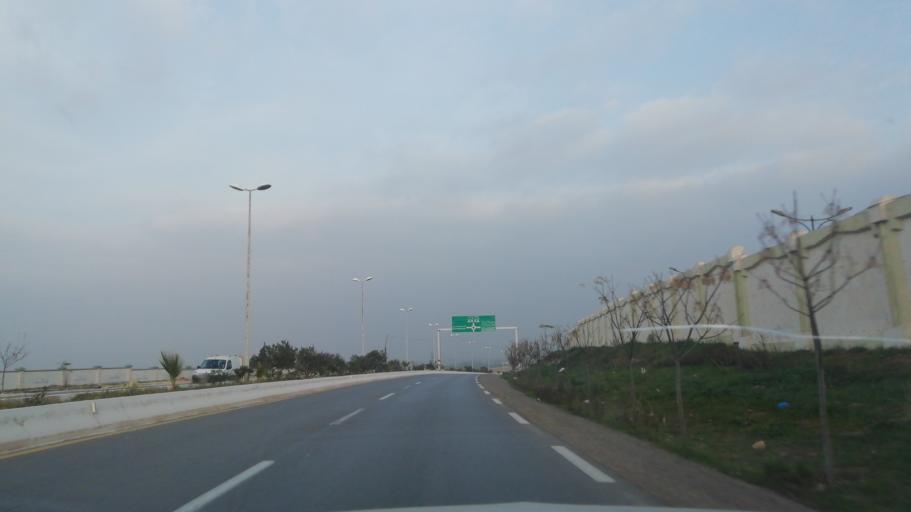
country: DZ
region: Sidi Bel Abbes
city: Sidi Bel Abbes
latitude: 35.2250
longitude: -0.6413
